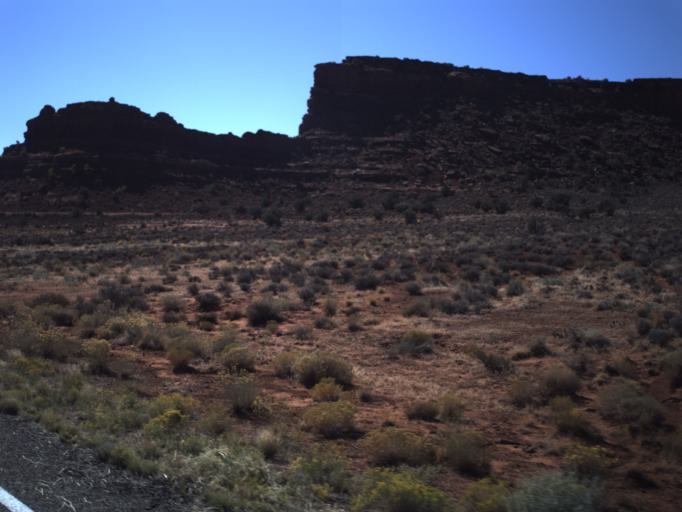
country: US
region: Utah
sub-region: San Juan County
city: Blanding
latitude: 37.7872
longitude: -110.2964
